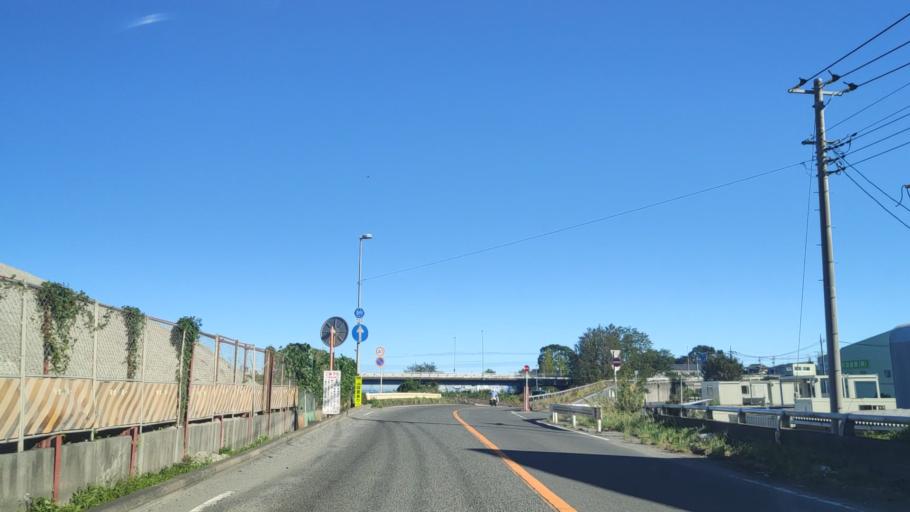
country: JP
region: Kanagawa
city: Zama
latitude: 35.5215
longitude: 139.3585
